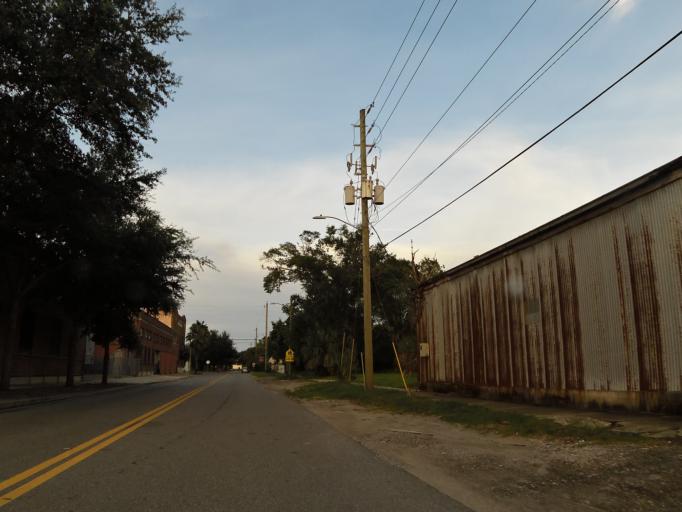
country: US
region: Florida
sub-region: Duval County
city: Jacksonville
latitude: 30.3508
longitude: -81.6596
